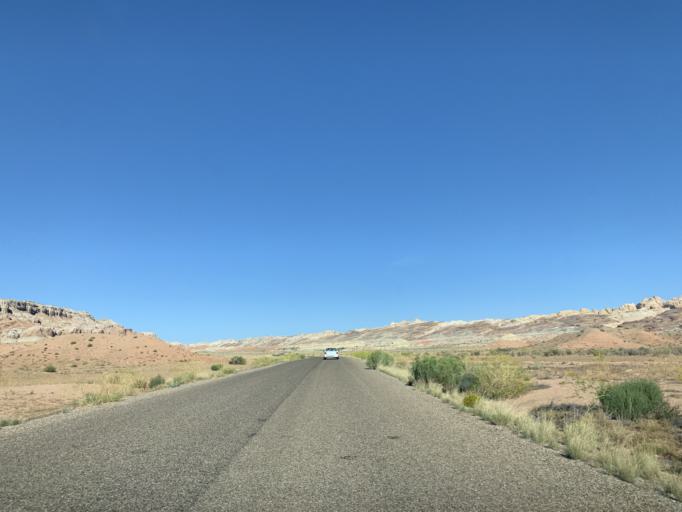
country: US
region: Utah
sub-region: Emery County
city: Ferron
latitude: 38.5751
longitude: -110.7519
